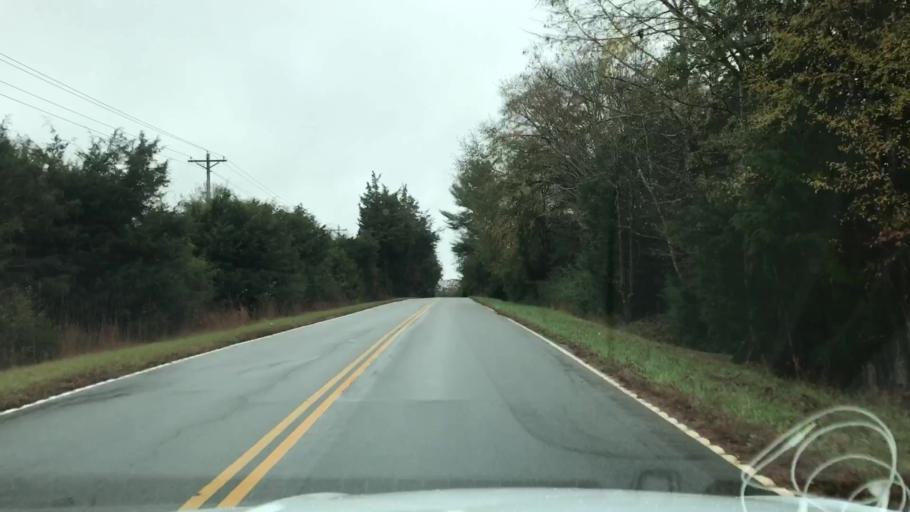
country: US
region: South Carolina
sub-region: Spartanburg County
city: Woodruff
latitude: 34.7581
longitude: -81.9230
